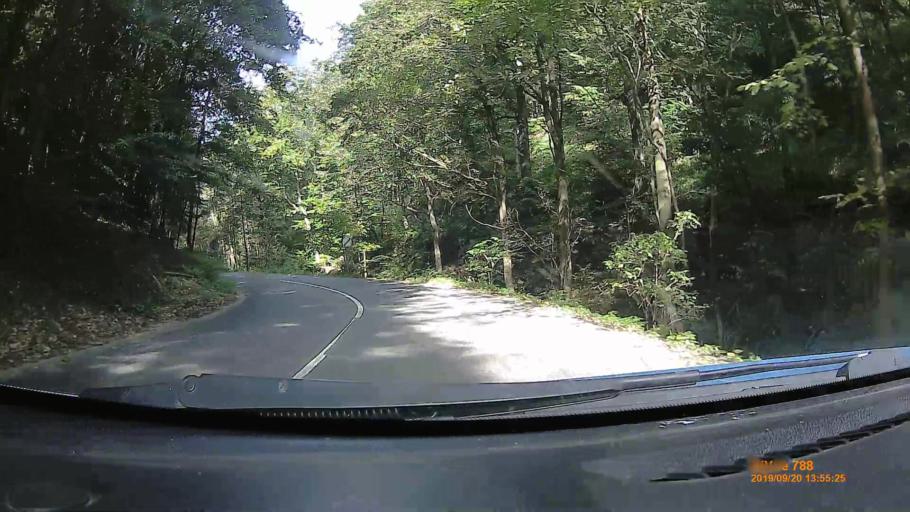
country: HU
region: Borsod-Abauj-Zemplen
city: Saly
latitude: 48.0810
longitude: 20.6158
